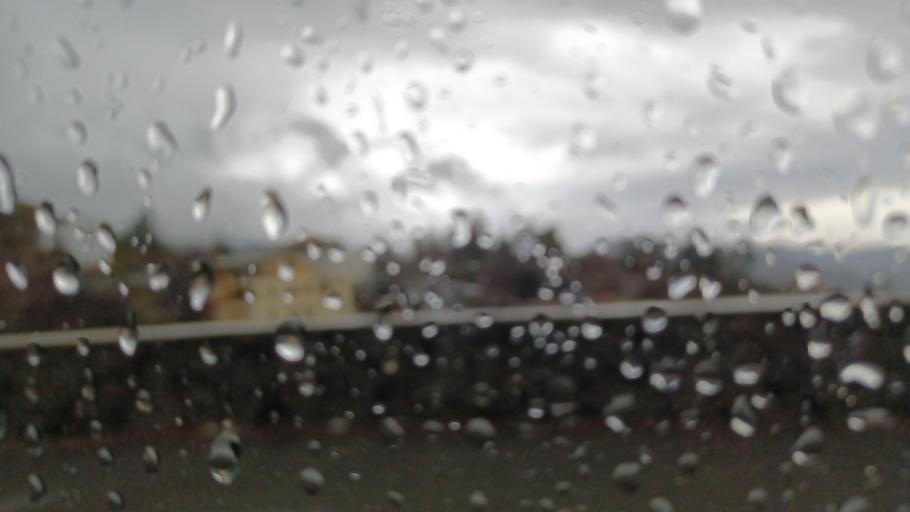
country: CY
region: Limassol
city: Kyperounta
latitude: 34.9453
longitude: 32.9798
